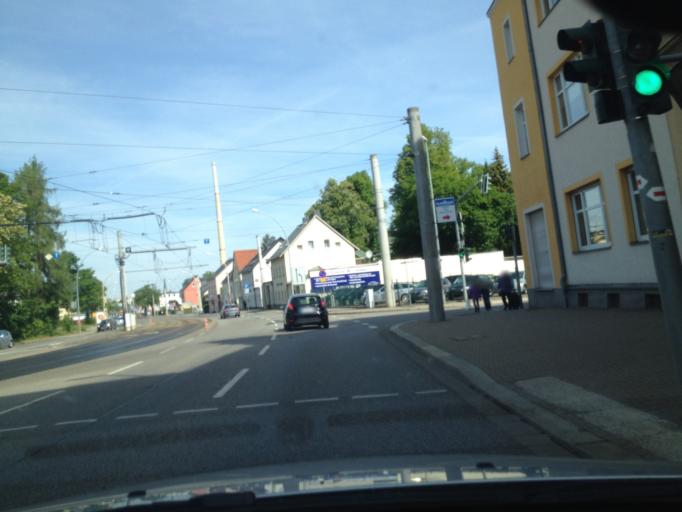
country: DE
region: Saxony
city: Chemnitz
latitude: 50.7916
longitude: 12.9268
